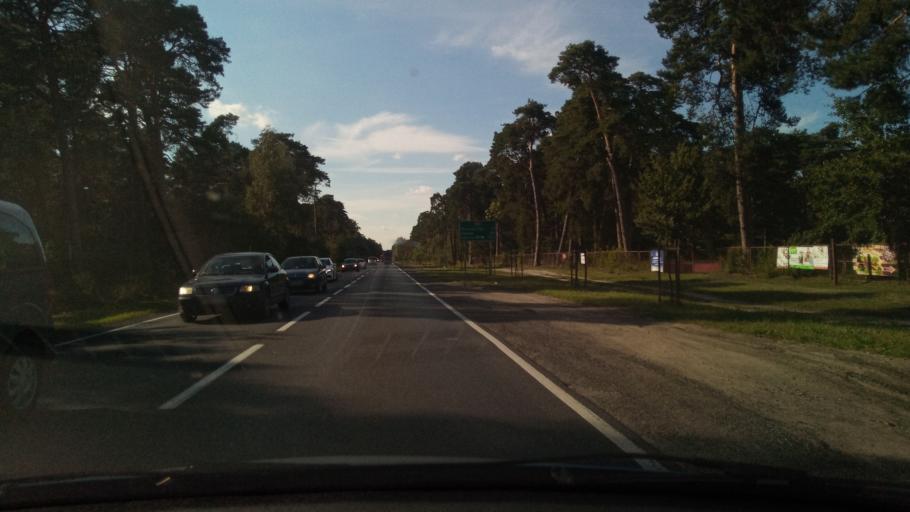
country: PL
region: Lodz Voivodeship
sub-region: Powiat piotrkowski
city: Sulejow
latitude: 51.3614
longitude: 19.8625
